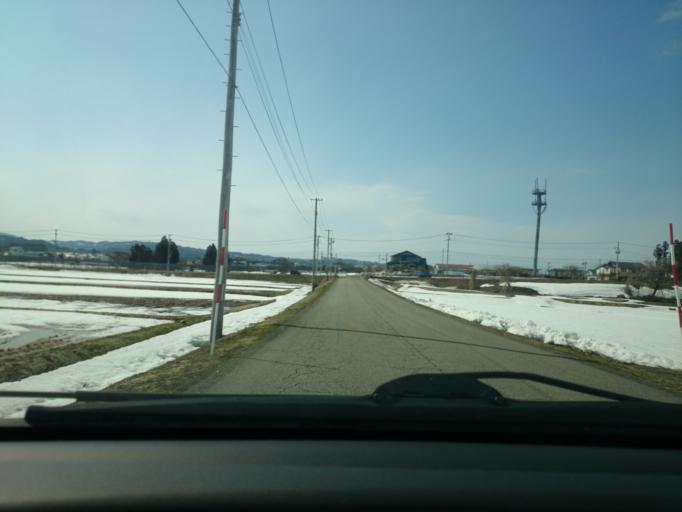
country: JP
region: Fukushima
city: Kitakata
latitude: 37.5167
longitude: 139.8363
